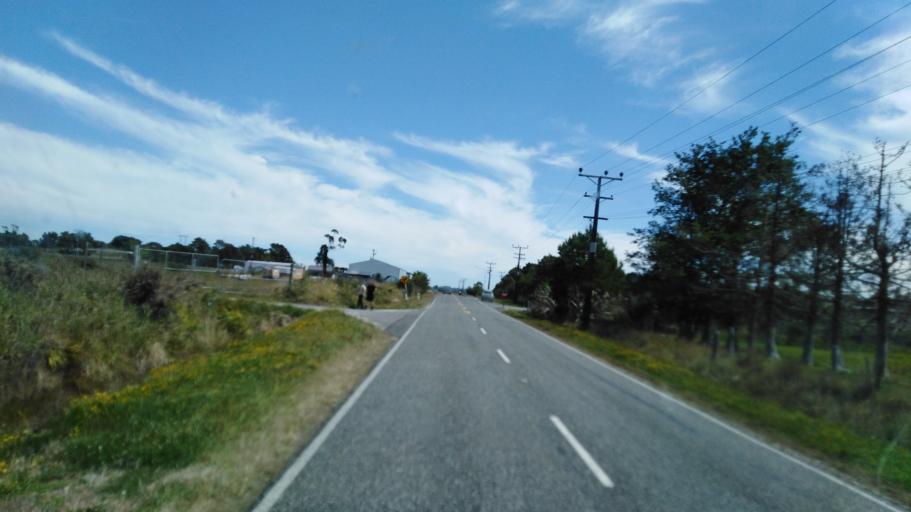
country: NZ
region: West Coast
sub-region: Buller District
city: Westport
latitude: -41.7591
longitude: 171.6491
